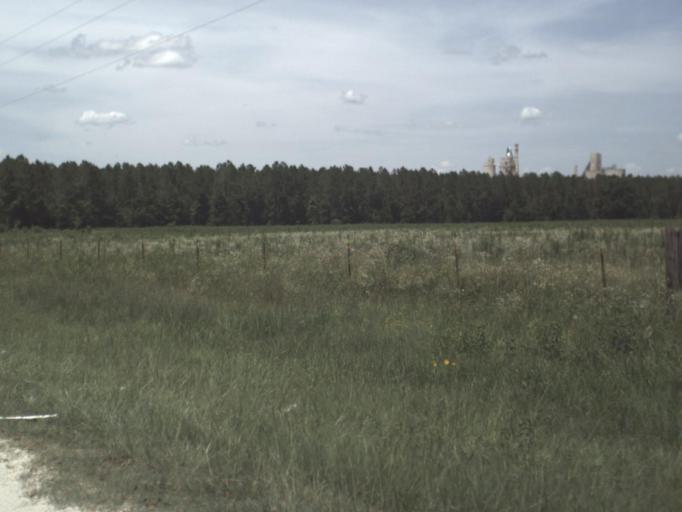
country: US
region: Florida
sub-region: Suwannee County
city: Wellborn
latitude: 29.9536
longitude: -82.8605
